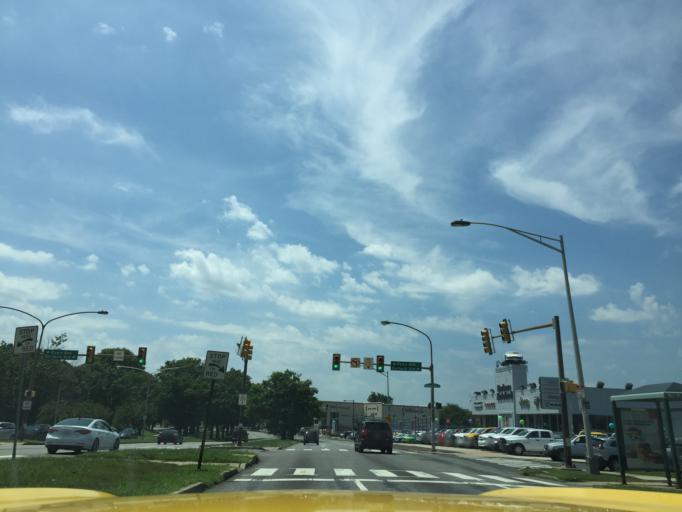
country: US
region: Pennsylvania
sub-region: Montgomery County
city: Rockledge
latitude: 40.0545
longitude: -75.0492
